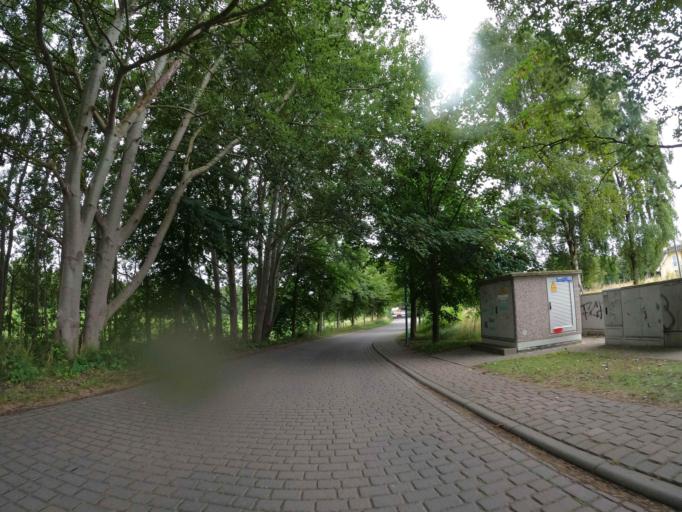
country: DE
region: Mecklenburg-Vorpommern
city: Ostseebad Gohren
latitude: 54.3222
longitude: 13.7268
